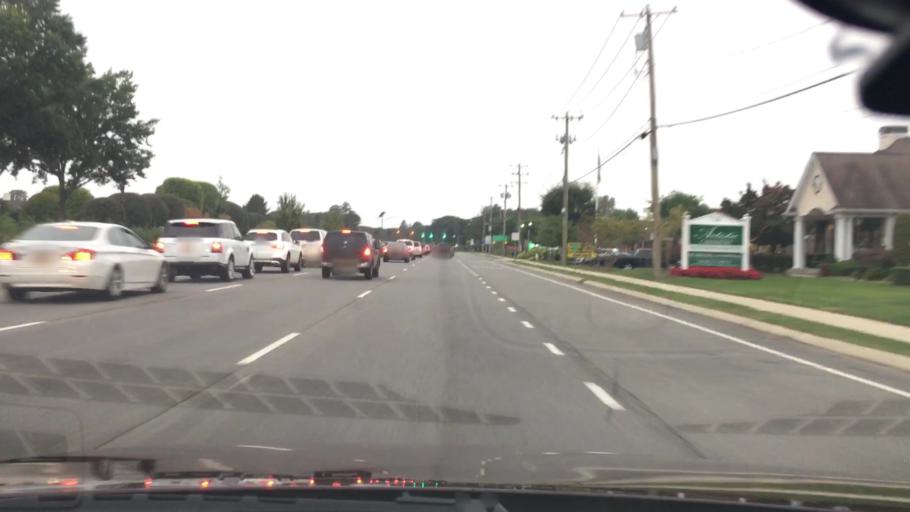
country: US
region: New York
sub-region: Suffolk County
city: Nesconset
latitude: 40.8492
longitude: -73.1670
